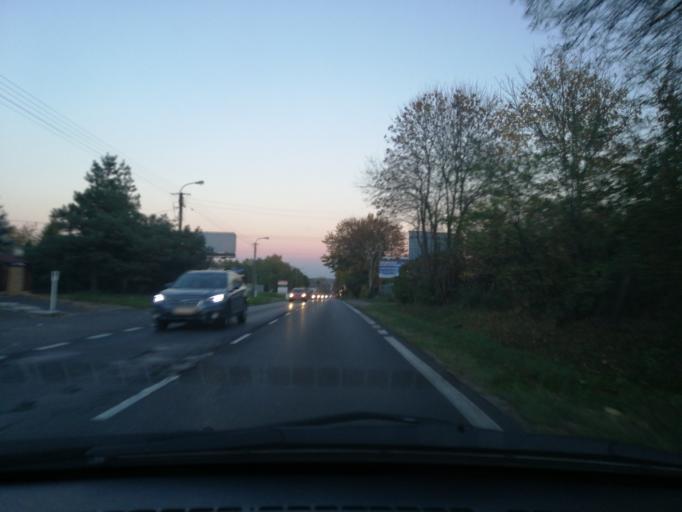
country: PL
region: Lodz Voivodeship
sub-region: Powiat lodzki wschodni
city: Andrespol
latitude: 51.7945
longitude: 19.5801
